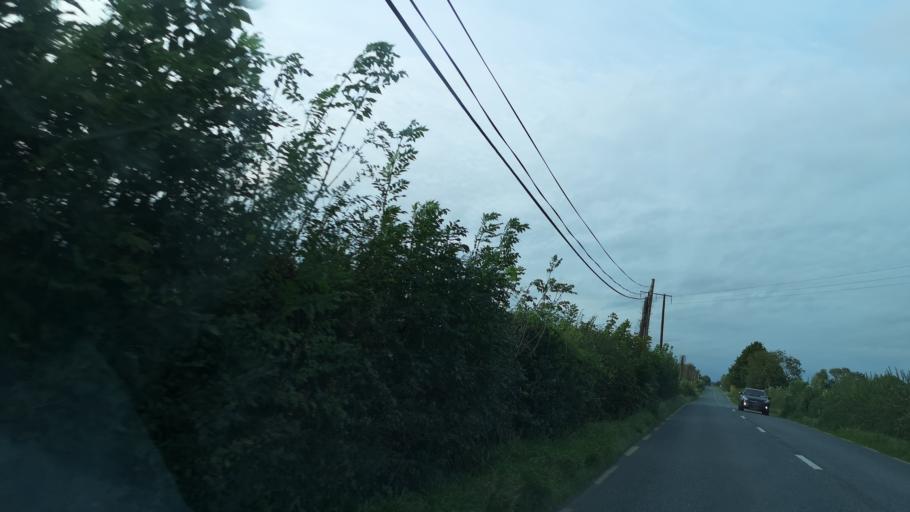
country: IE
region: Leinster
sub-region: Uibh Fhaili
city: Ferbane
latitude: 53.3173
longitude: -7.8212
